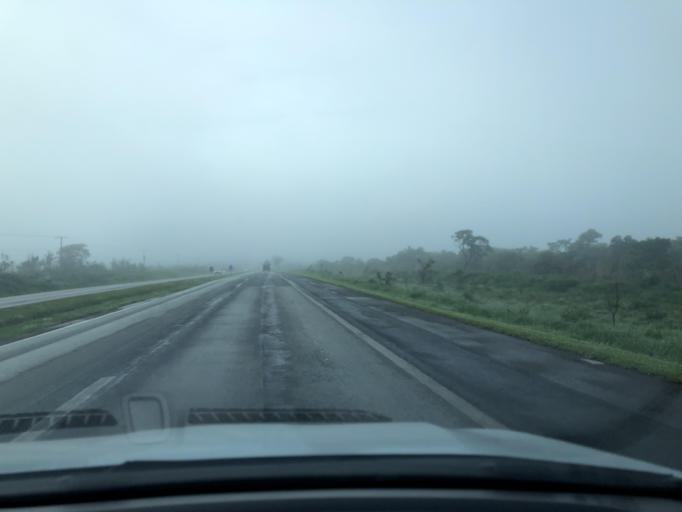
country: BR
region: Goias
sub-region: Luziania
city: Luziania
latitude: -16.2910
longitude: -47.8527
